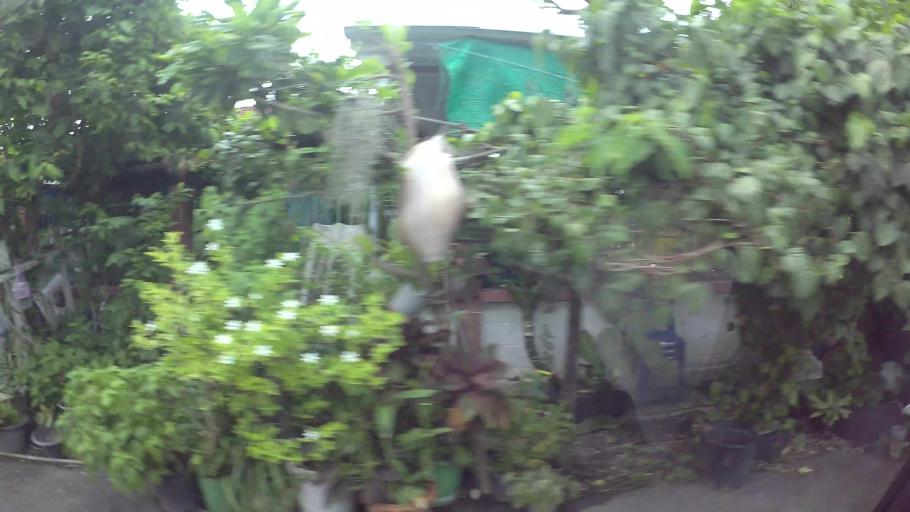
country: TH
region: Chon Buri
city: Sattahip
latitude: 12.6847
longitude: 100.9012
